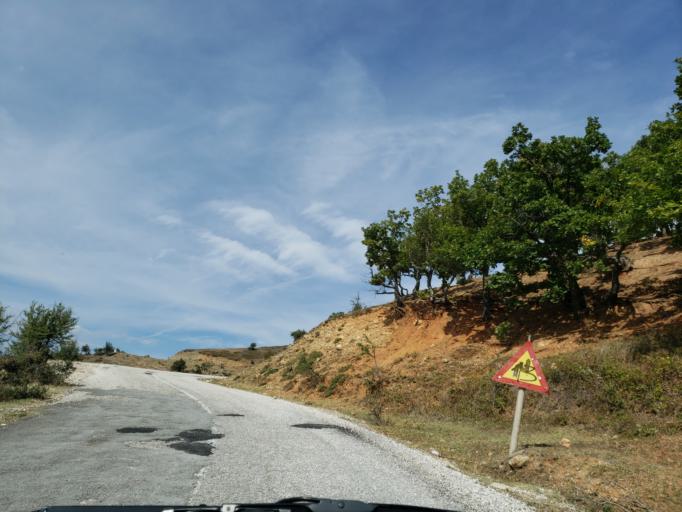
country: GR
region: Thessaly
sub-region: Trikala
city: Kastraki
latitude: 39.7501
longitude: 21.6614
